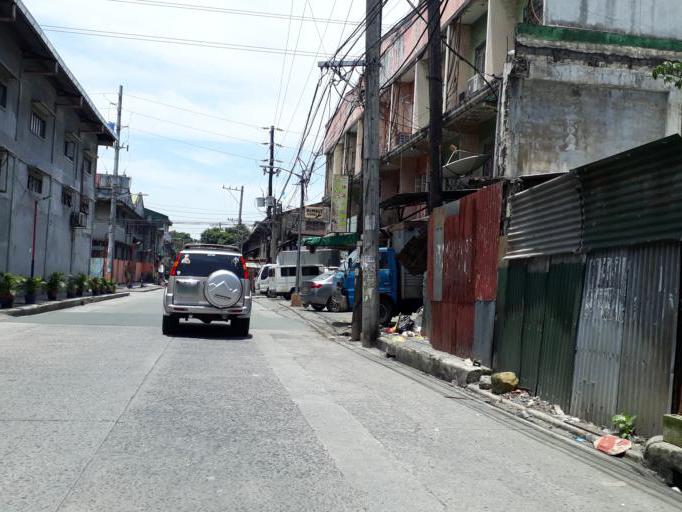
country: PH
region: Metro Manila
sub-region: Caloocan City
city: Niugan
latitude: 14.6461
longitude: 120.9821
